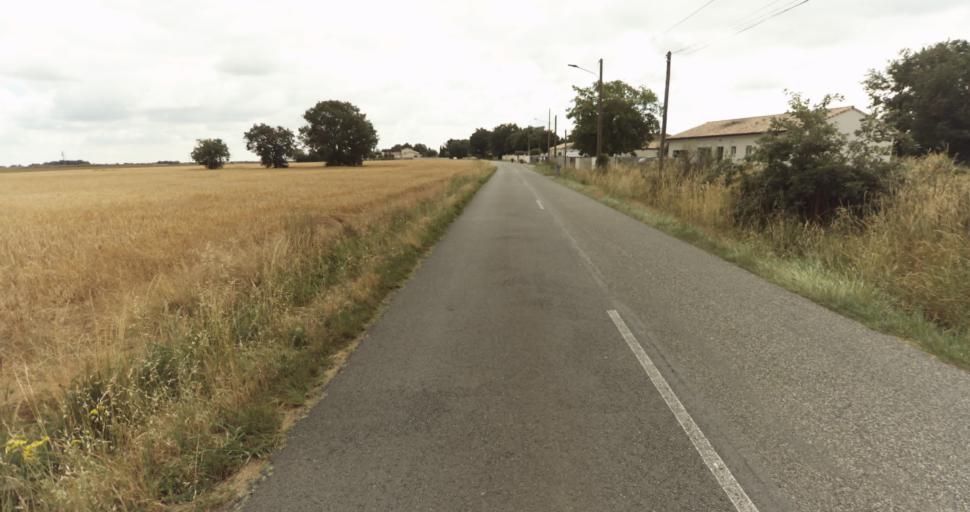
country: FR
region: Midi-Pyrenees
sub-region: Departement de la Haute-Garonne
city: Fonsorbes
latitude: 43.5494
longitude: 1.2154
